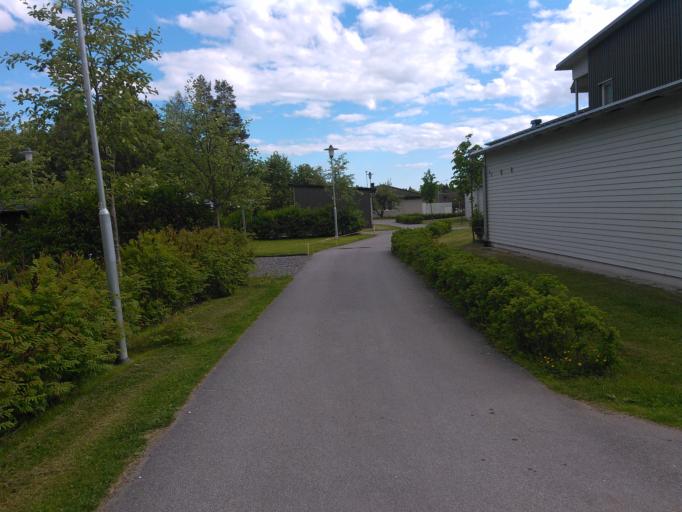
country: SE
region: Vaesterbotten
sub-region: Umea Kommun
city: Umea
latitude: 63.7989
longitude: 20.3120
